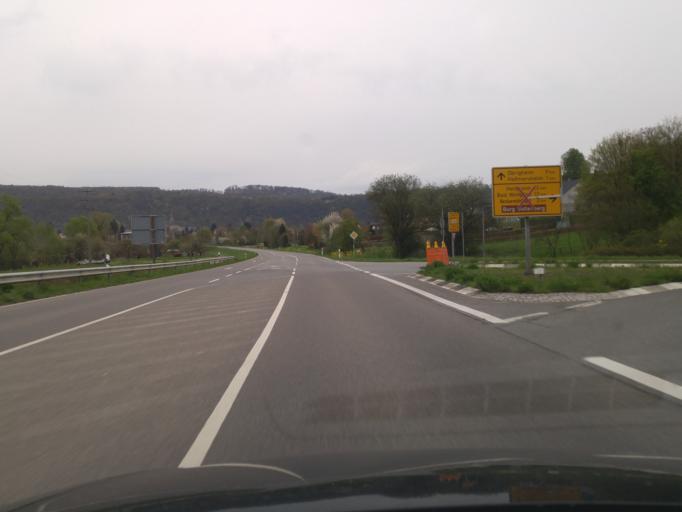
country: DE
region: Baden-Wuerttemberg
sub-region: Karlsruhe Region
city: Hassmersheim
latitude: 49.3004
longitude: 9.1357
